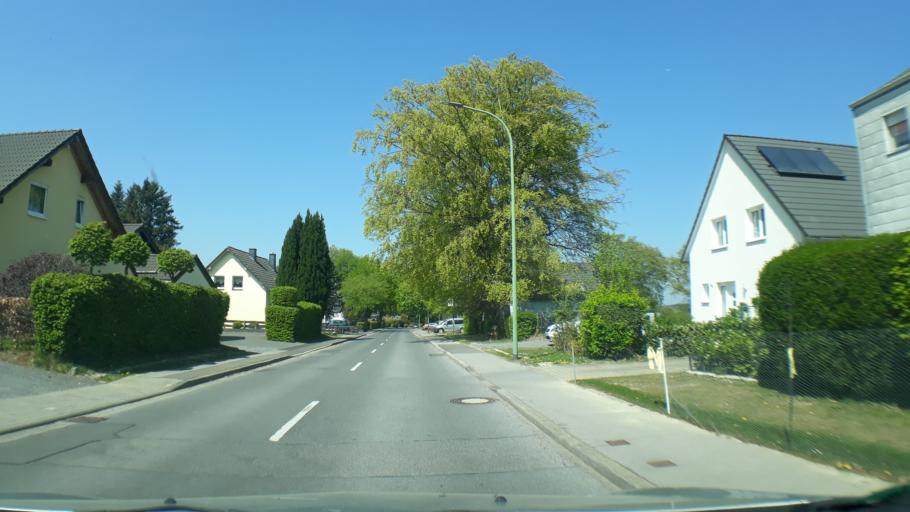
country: DE
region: North Rhine-Westphalia
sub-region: Regierungsbezirk Koln
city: Roetgen
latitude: 50.6417
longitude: 6.2021
